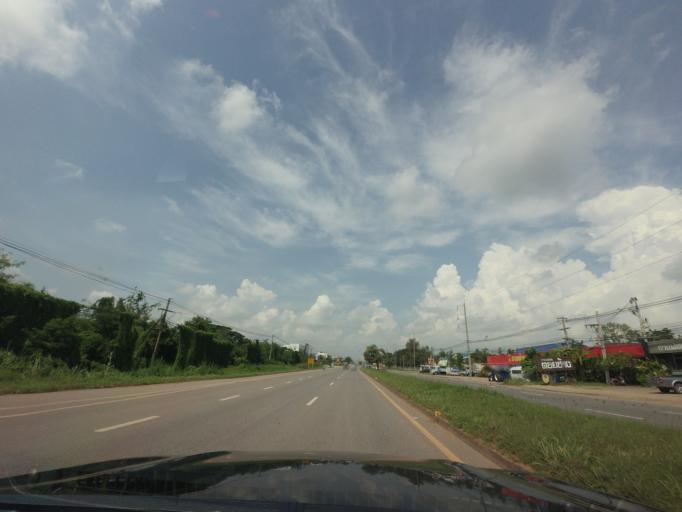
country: TH
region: Khon Kaen
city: Ban Fang
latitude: 16.4504
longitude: 102.7305
